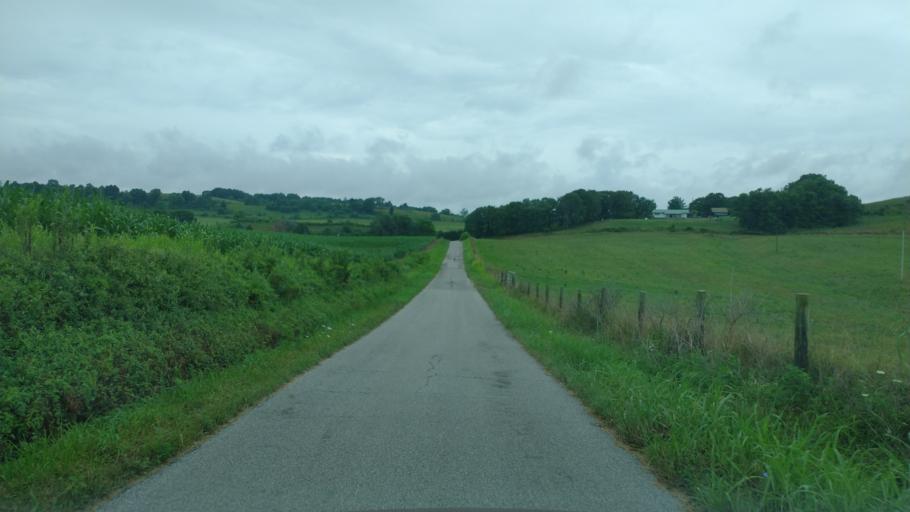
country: US
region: West Virginia
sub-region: Mason County
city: New Haven
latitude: 38.9243
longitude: -81.9510
